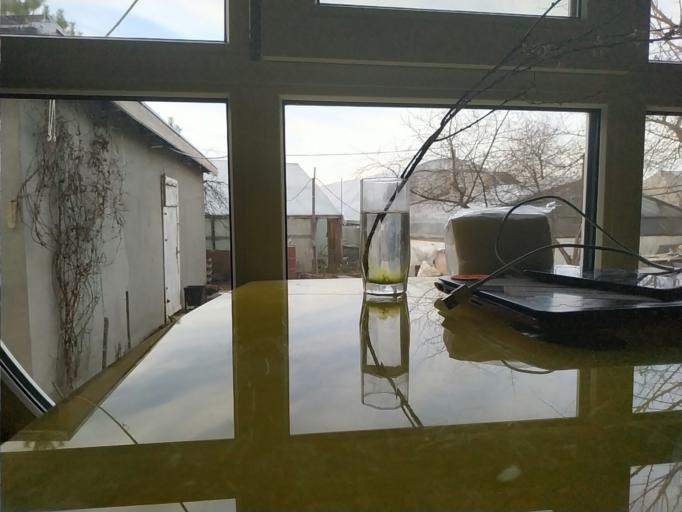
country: RU
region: Republic of Karelia
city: Suoyarvi
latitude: 61.8692
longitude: 32.2694
